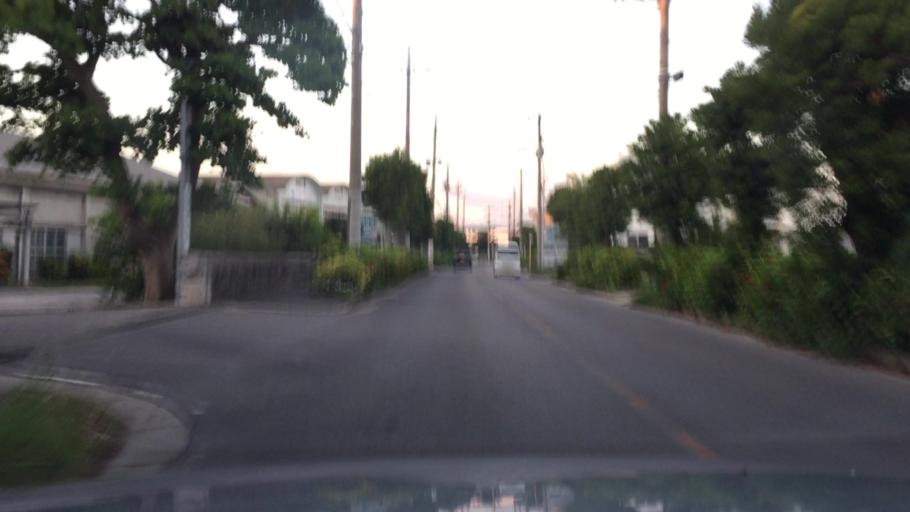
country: JP
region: Okinawa
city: Ishigaki
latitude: 24.3468
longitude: 124.1620
